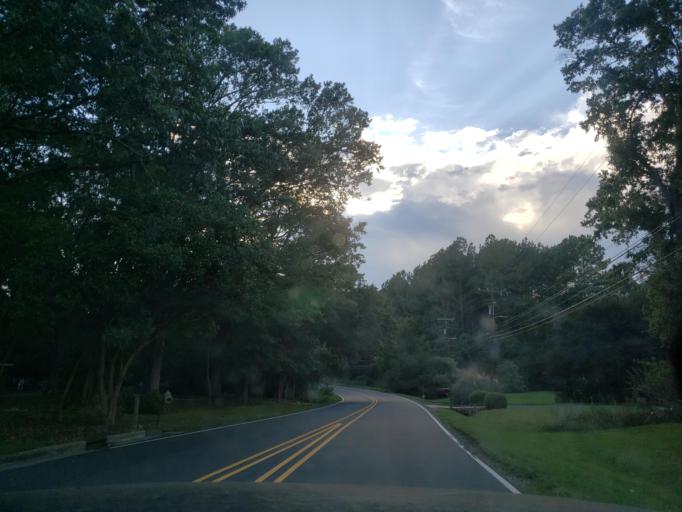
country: US
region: North Carolina
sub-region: Durham County
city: Durham
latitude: 35.9925
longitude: -78.9819
